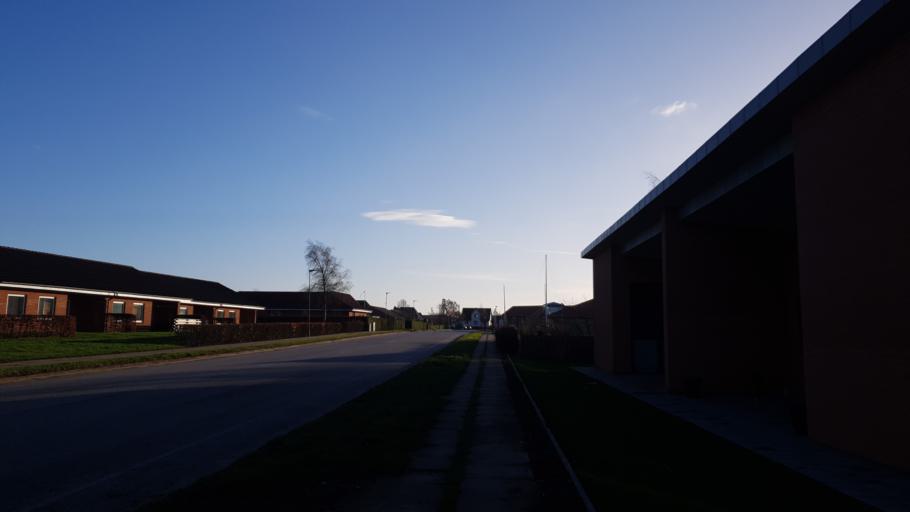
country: DK
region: Central Jutland
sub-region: Hedensted Kommune
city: Hedensted
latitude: 55.8063
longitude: 9.6920
